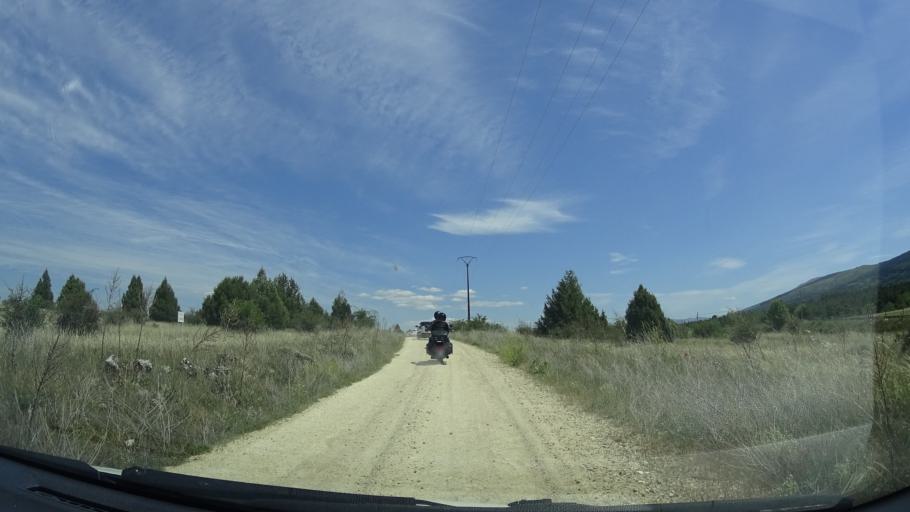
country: ES
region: Castille and Leon
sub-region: Provincia de Segovia
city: Pradena
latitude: 41.1433
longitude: -3.6779
